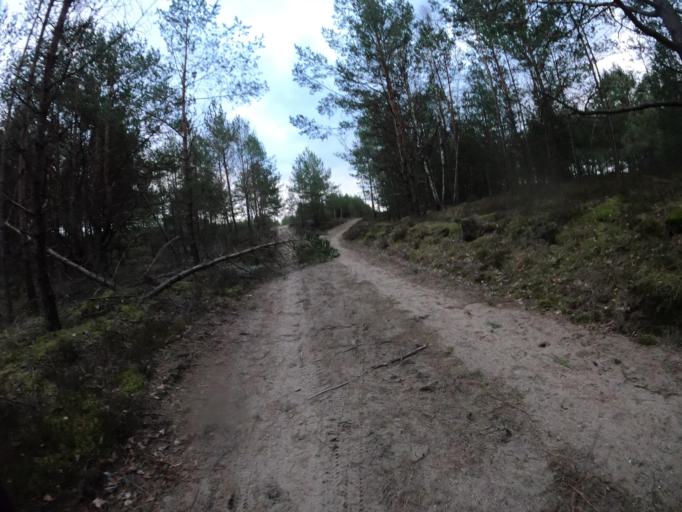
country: PL
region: West Pomeranian Voivodeship
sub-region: Powiat szczecinecki
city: Borne Sulinowo
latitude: 53.5678
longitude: 16.5564
